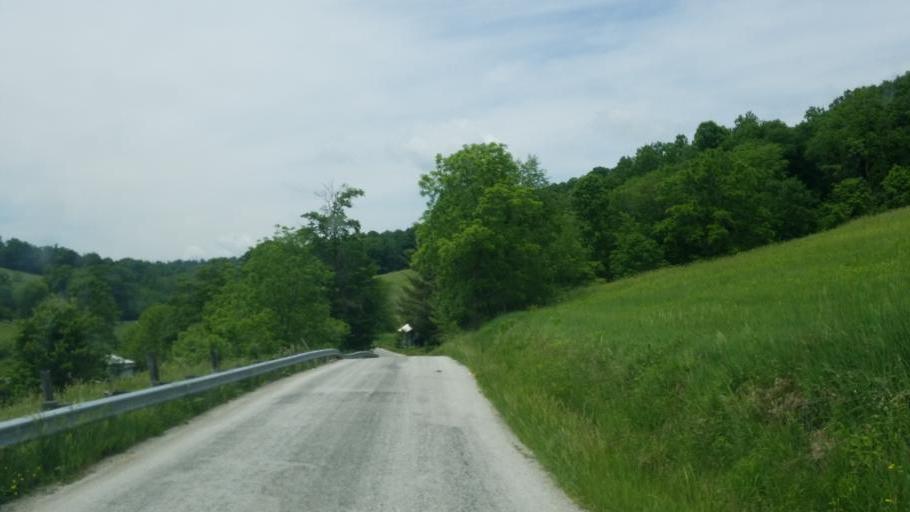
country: US
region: Ohio
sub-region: Coshocton County
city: West Lafayette
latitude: 40.3763
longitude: -81.7754
